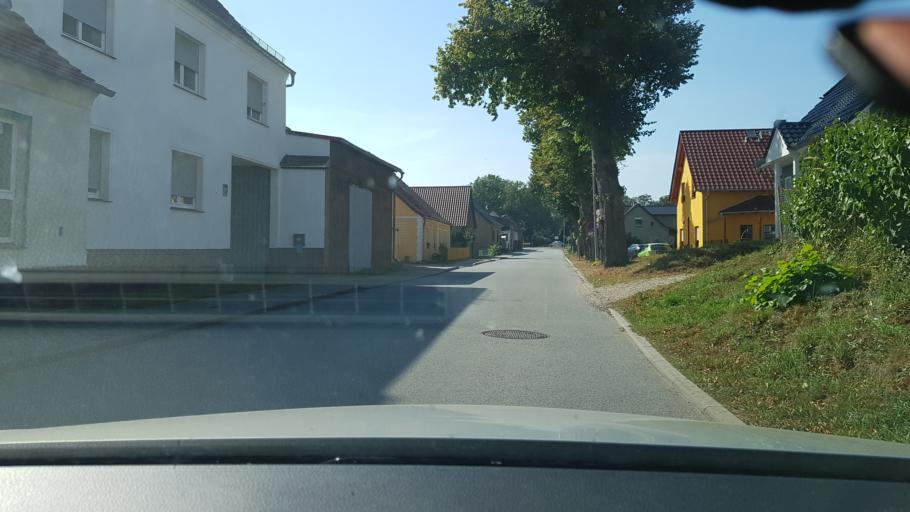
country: DE
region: Brandenburg
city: Lawitz
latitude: 52.1267
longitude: 14.5917
